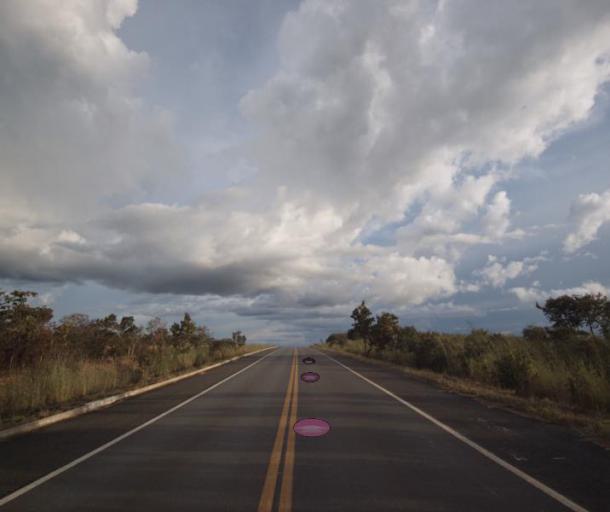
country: BR
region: Goias
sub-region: Barro Alto
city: Barro Alto
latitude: -14.8251
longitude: -48.6384
